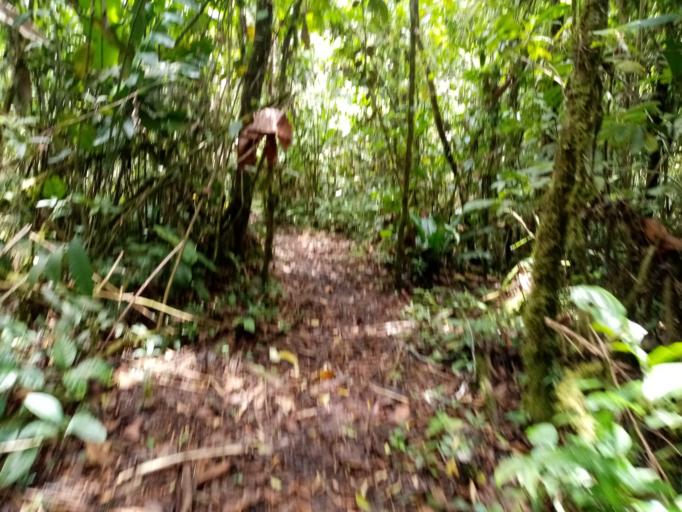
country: EC
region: Napo
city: Tena
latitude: -0.9710
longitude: -77.7981
